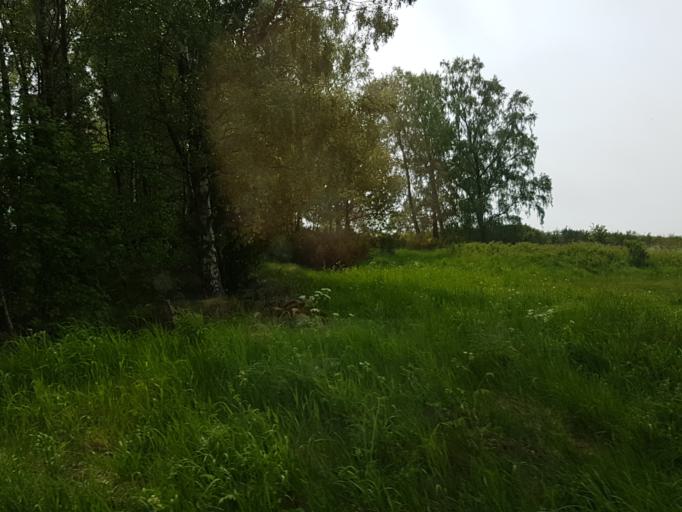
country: SE
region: Skane
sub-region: Tomelilla Kommun
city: Tomelilla
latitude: 55.5116
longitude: 14.0196
